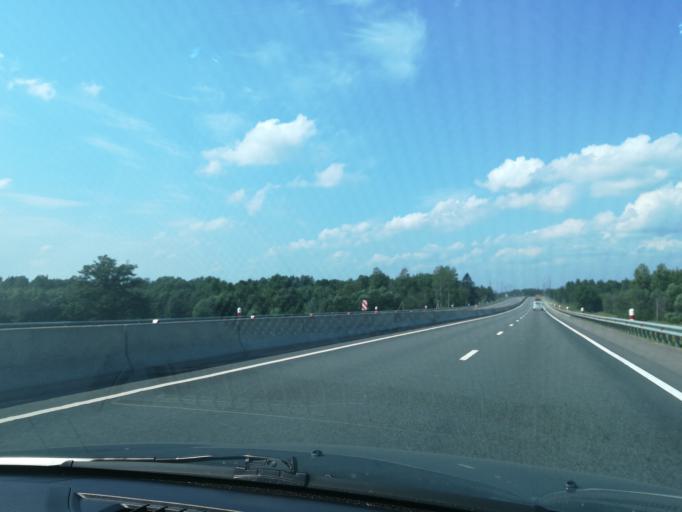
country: RU
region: Leningrad
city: Kingisepp
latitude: 59.5957
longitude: 28.7325
